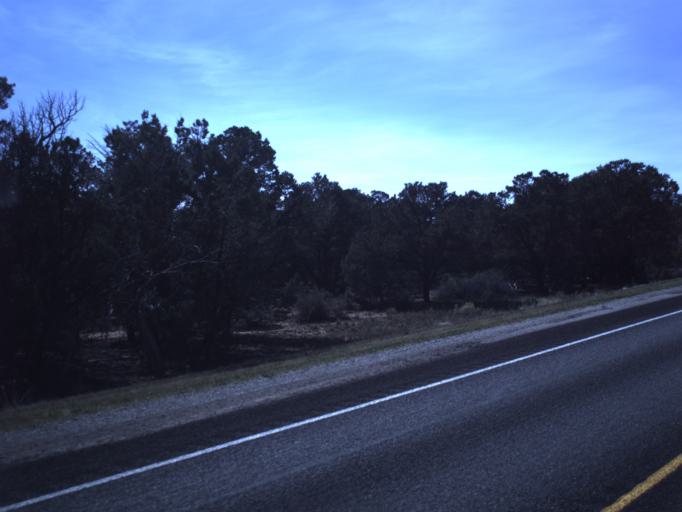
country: US
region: Utah
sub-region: San Juan County
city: Monticello
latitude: 37.8404
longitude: -109.1252
